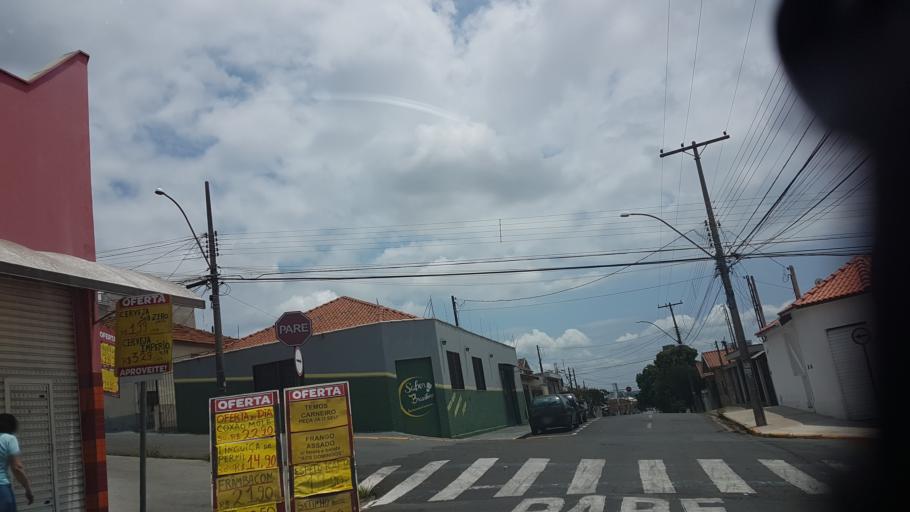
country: BR
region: Sao Paulo
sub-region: Piracicaba
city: Piracicaba
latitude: -22.7422
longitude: -47.6540
